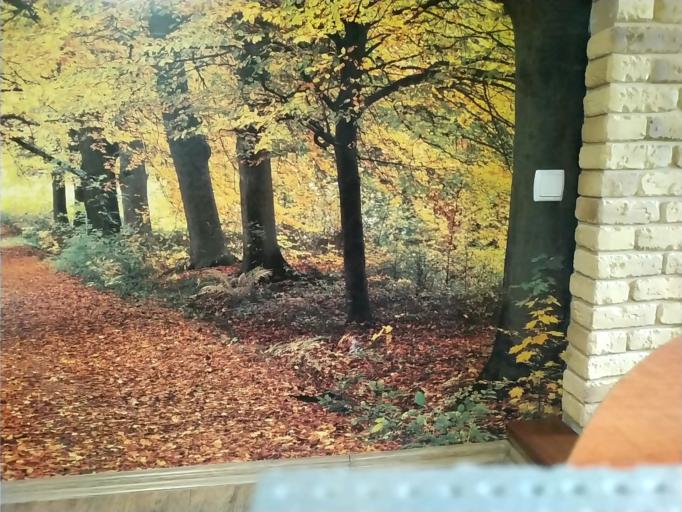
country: RU
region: Tverskaya
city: Staritsa
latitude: 56.5278
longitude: 35.0429
